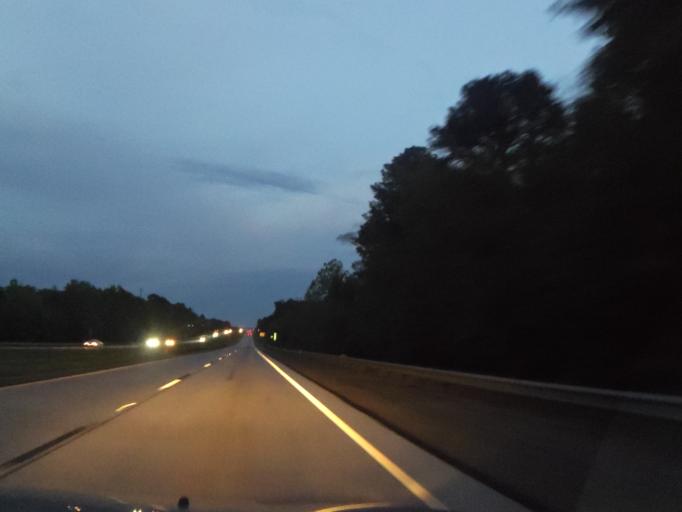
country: US
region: Georgia
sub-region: McDuffie County
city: Thomson
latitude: 33.5124
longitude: -82.4602
